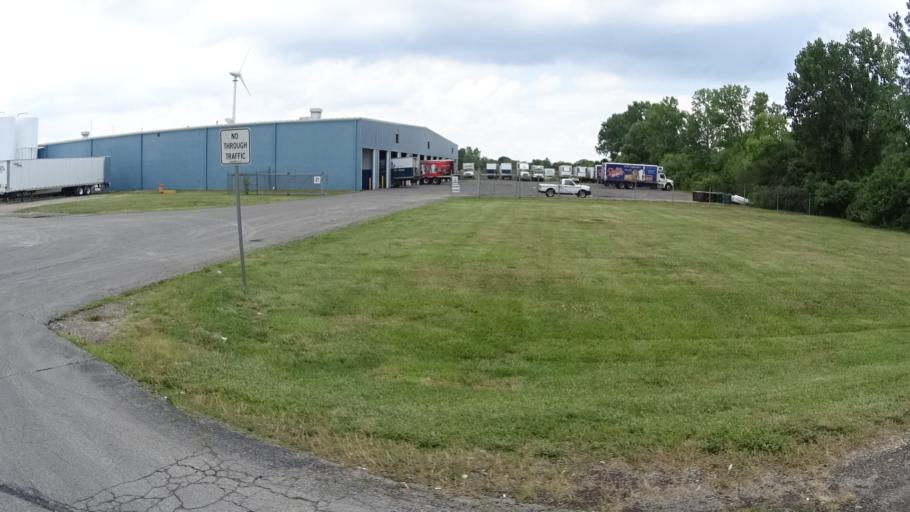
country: US
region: Ohio
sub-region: Erie County
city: Sandusky
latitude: 41.4433
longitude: -82.7514
